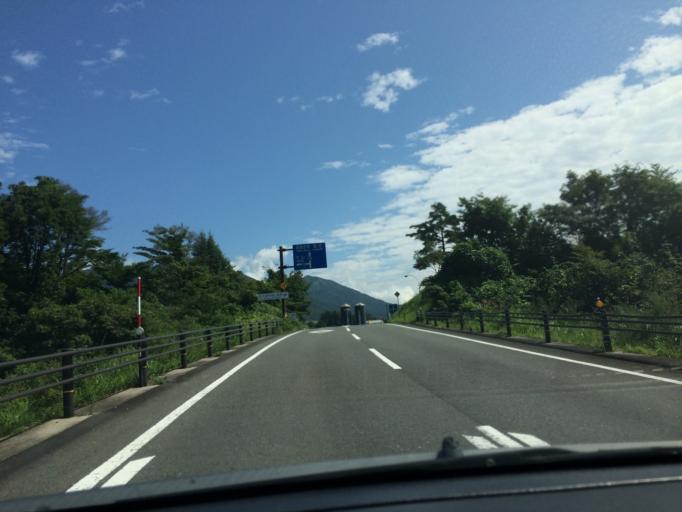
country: JP
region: Tottori
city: Kurayoshi
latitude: 35.2984
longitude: 133.6268
